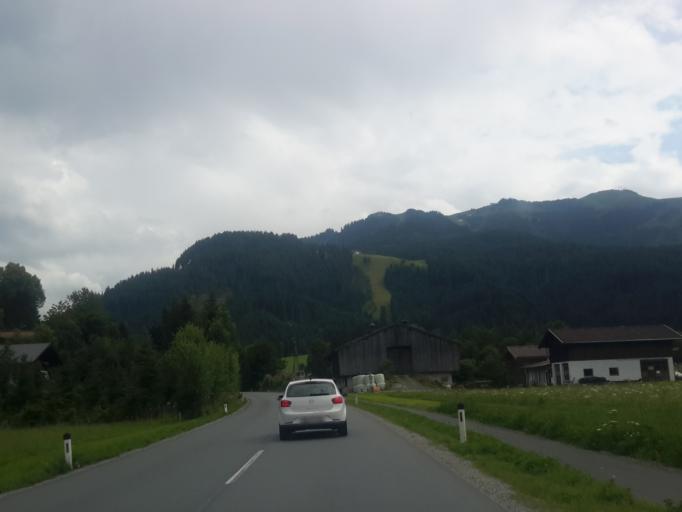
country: AT
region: Tyrol
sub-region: Politischer Bezirk Kitzbuhel
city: Reith bei Kitzbuhel
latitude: 47.4629
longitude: 12.3532
